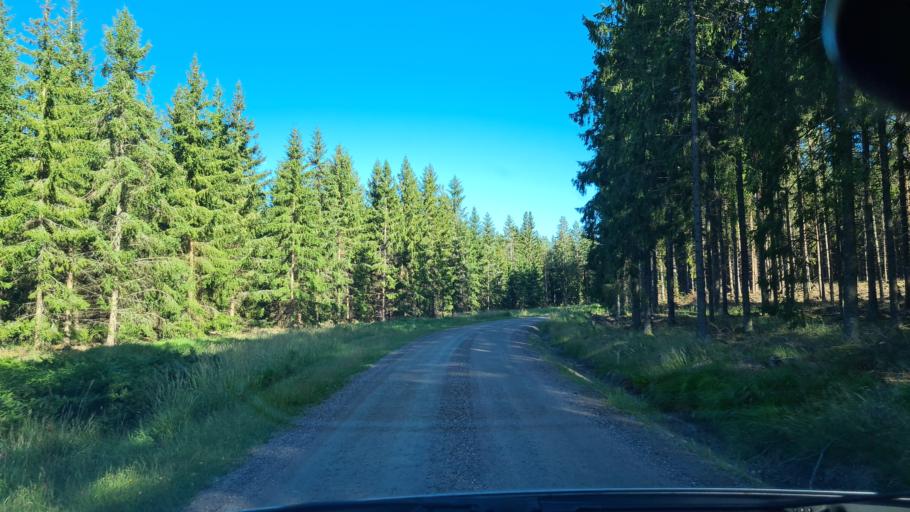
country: SE
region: Soedermanland
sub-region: Nykopings Kommun
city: Stigtomta
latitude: 58.9239
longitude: 16.9036
